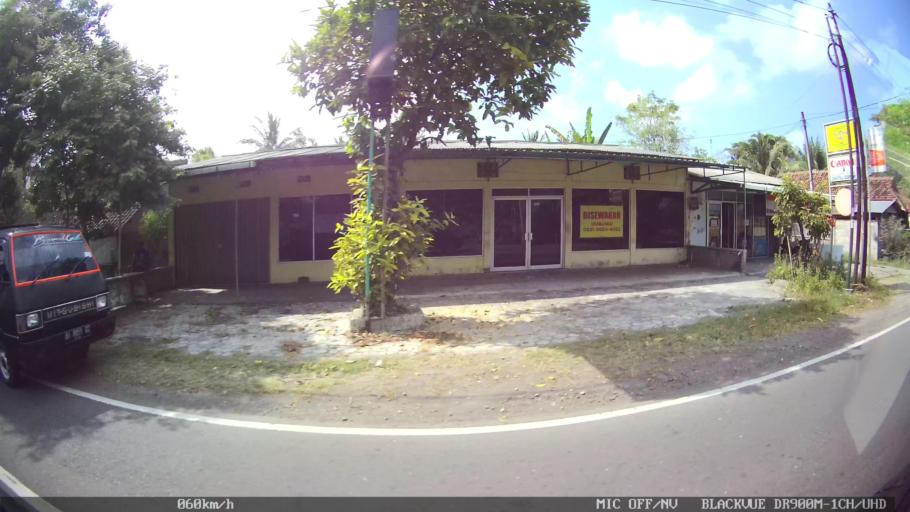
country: ID
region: Daerah Istimewa Yogyakarta
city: Srandakan
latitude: -7.8755
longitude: 110.1354
